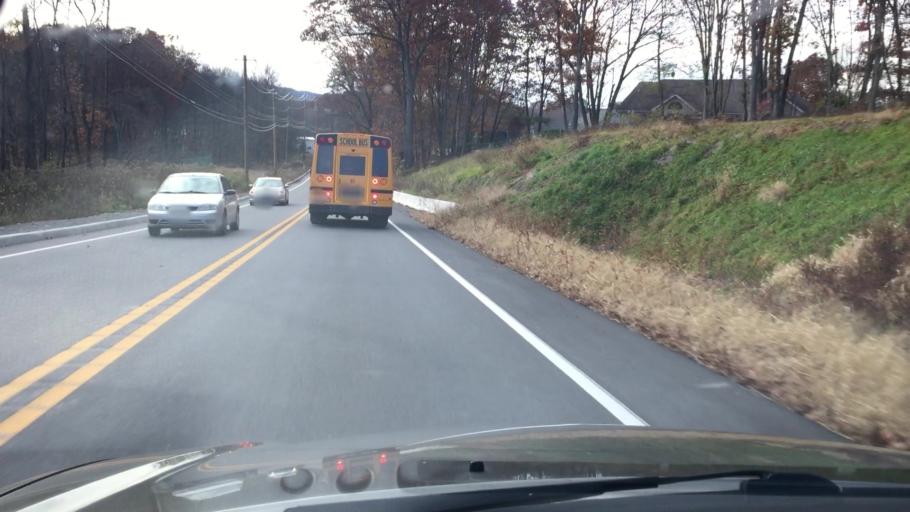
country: US
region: Pennsylvania
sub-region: Luzerne County
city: Nanticoke
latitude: 41.1929
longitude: -75.9820
